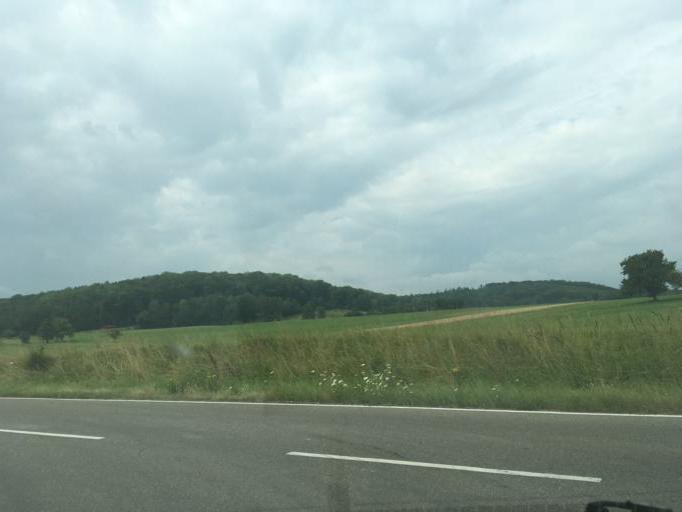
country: DE
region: Baden-Wuerttemberg
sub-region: Regierungsbezirk Stuttgart
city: Waldenbuch
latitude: 48.6287
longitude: 9.1318
